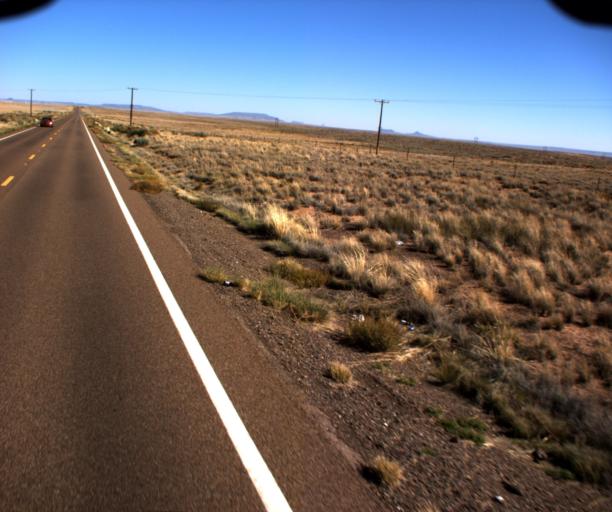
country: US
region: Arizona
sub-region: Navajo County
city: Winslow
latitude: 35.0711
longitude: -110.5714
